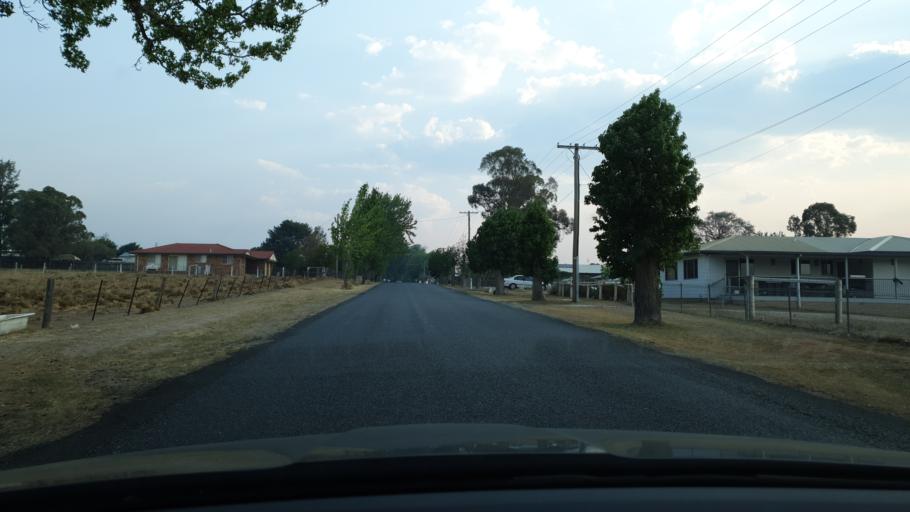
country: AU
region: New South Wales
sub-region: Tenterfield Municipality
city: Carrolls Creek
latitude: -29.0436
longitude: 152.0233
